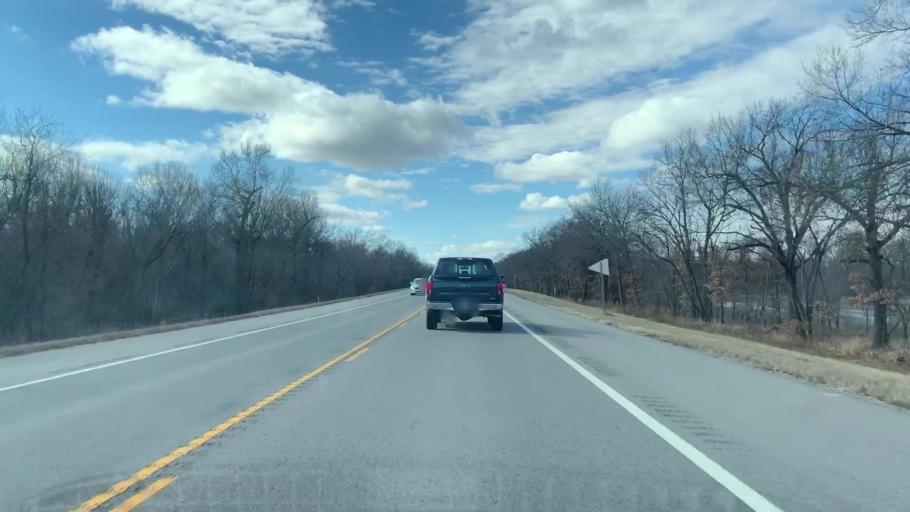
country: US
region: Kansas
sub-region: Cherokee County
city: Columbus
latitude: 37.3401
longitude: -94.9691
